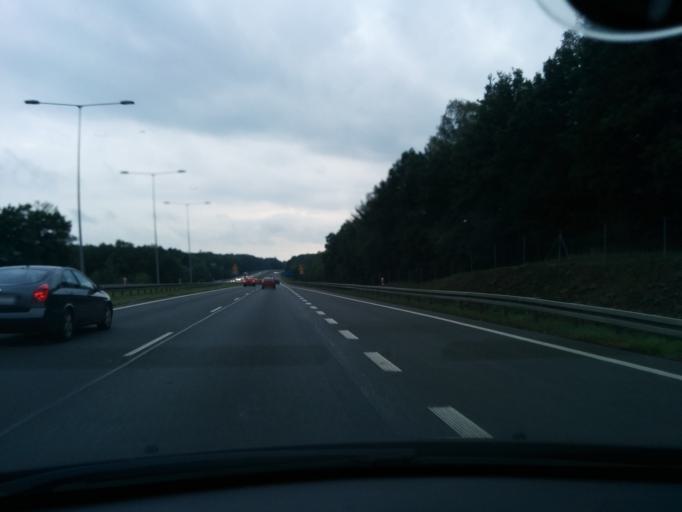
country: PL
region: Silesian Voivodeship
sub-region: Myslowice
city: Myslowice
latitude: 50.2183
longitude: 19.1183
